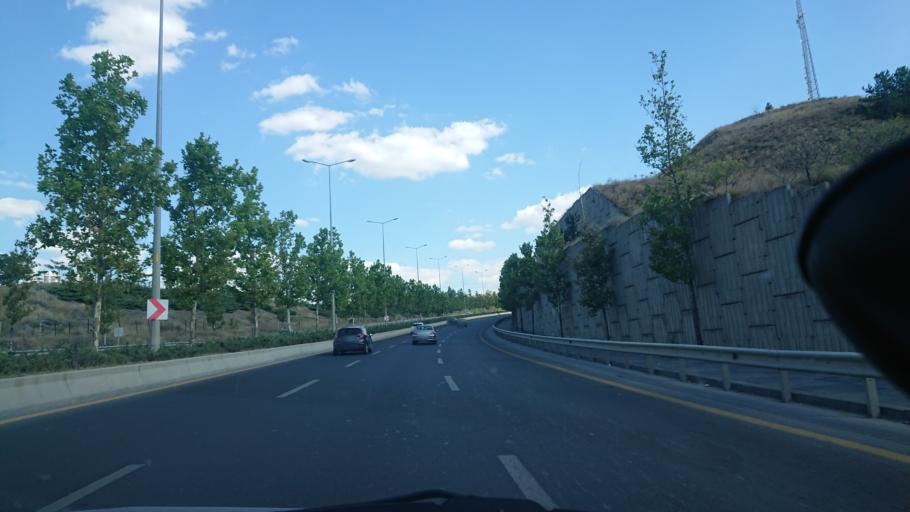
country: TR
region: Ankara
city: Mamak
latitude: 39.8881
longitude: 32.9122
